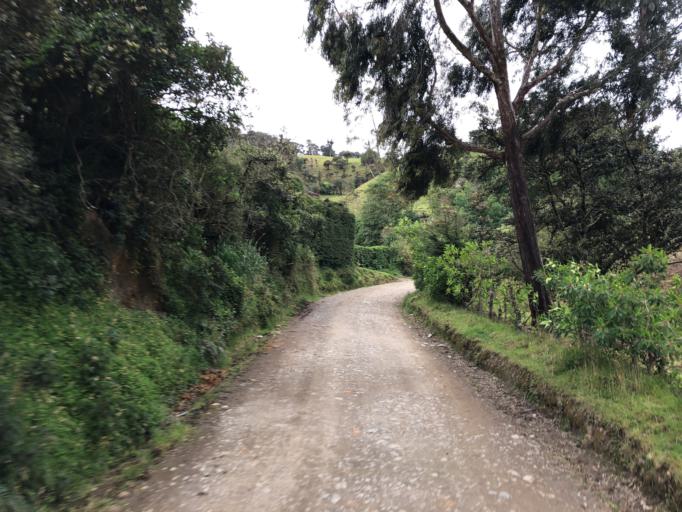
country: CO
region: Cauca
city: Totoro
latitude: 2.4972
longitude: -76.3543
